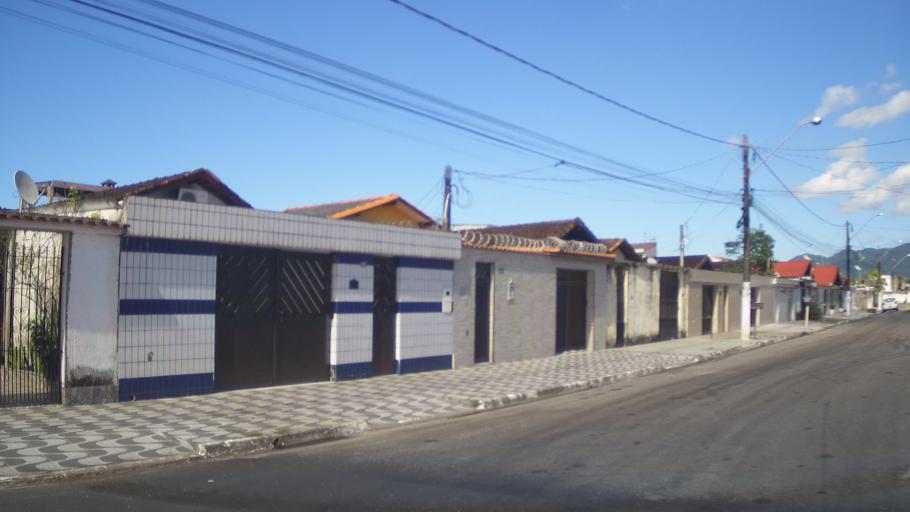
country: BR
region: Sao Paulo
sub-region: Mongagua
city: Mongagua
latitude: -24.0283
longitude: -46.5321
